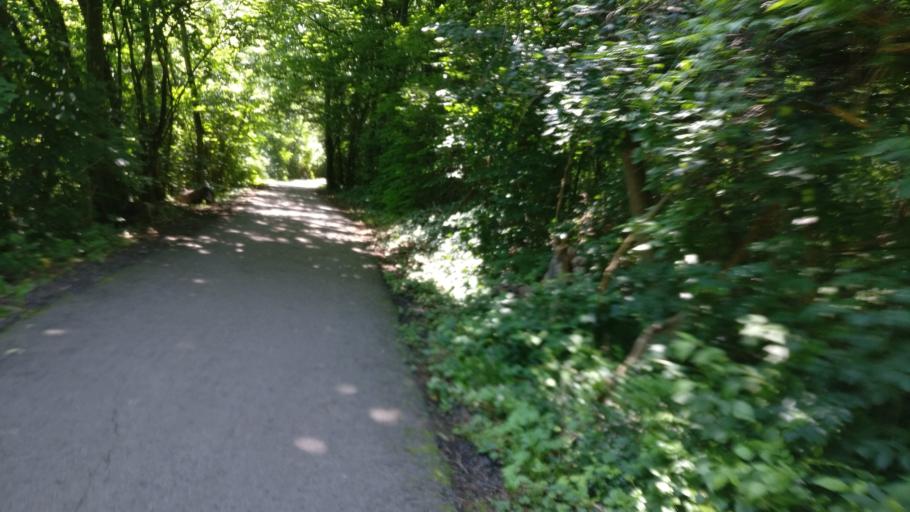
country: AT
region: Lower Austria
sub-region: Politischer Bezirk Baden
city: Oberwaltersdorf
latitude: 47.9649
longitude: 16.3106
